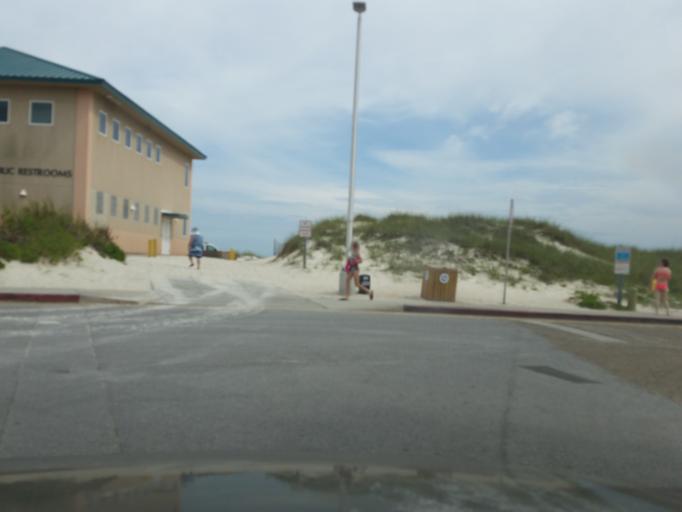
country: US
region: Florida
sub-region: Santa Rosa County
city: Gulf Breeze
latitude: 30.3316
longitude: -87.1421
